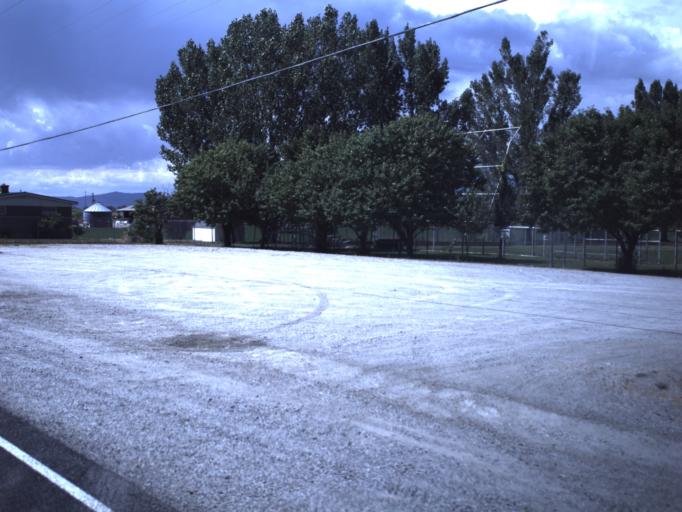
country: US
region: Utah
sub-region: Box Elder County
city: Honeyville
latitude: 41.6348
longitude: -112.0855
